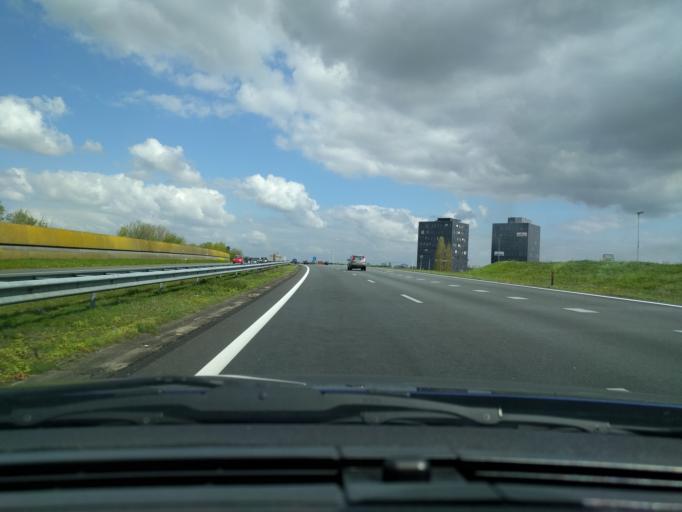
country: NL
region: North Brabant
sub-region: Gemeente Veghel
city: Eerde
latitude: 51.5962
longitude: 5.5106
